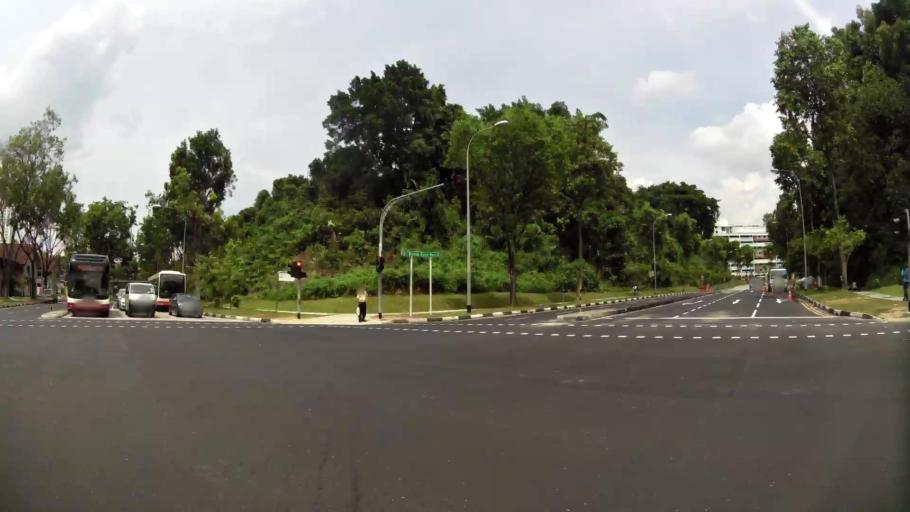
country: SG
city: Singapore
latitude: 1.3495
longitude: 103.7528
